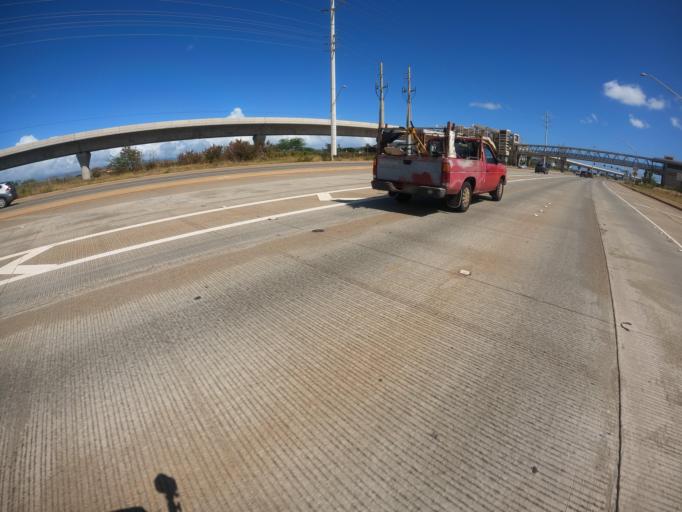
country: US
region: Hawaii
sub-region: Honolulu County
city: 'Ewa Villages
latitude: 21.3591
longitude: -158.0524
